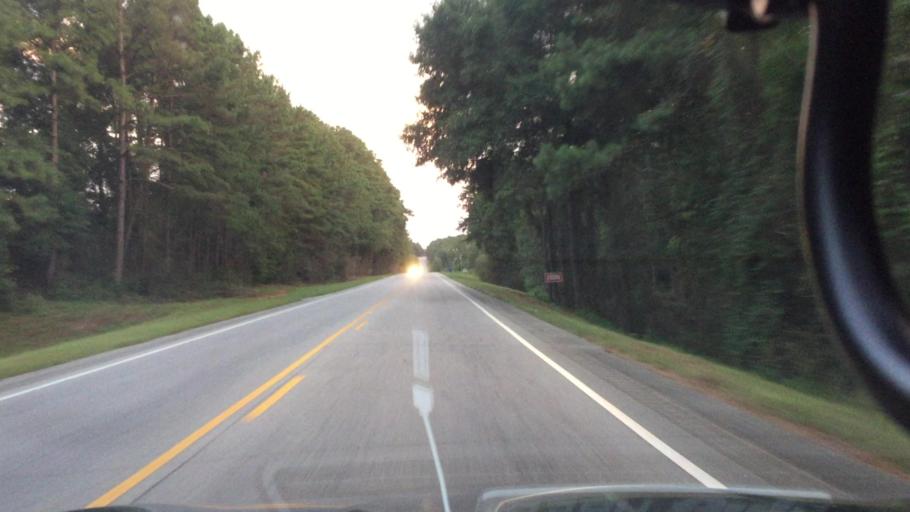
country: US
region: Alabama
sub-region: Coffee County
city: New Brockton
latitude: 31.3905
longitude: -85.8770
